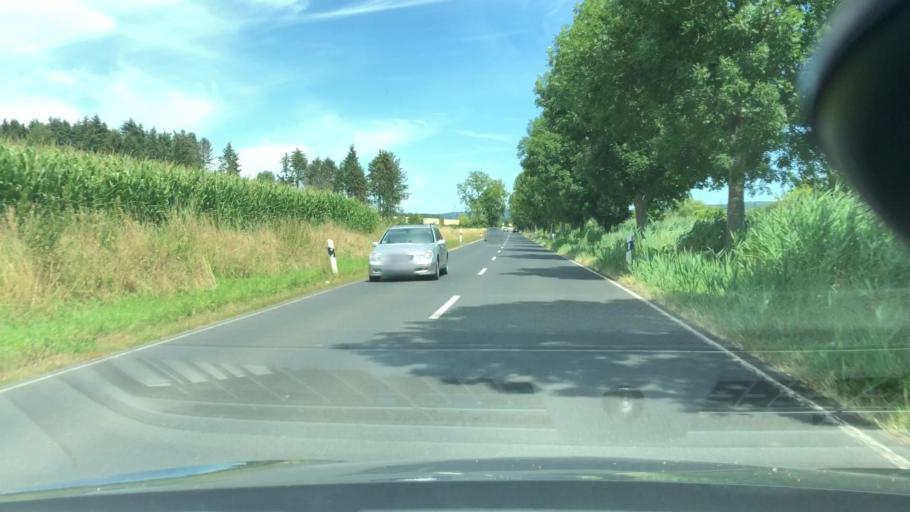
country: DE
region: Hesse
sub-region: Regierungsbezirk Darmstadt
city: Langenselbold
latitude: 50.2091
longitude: 9.0903
